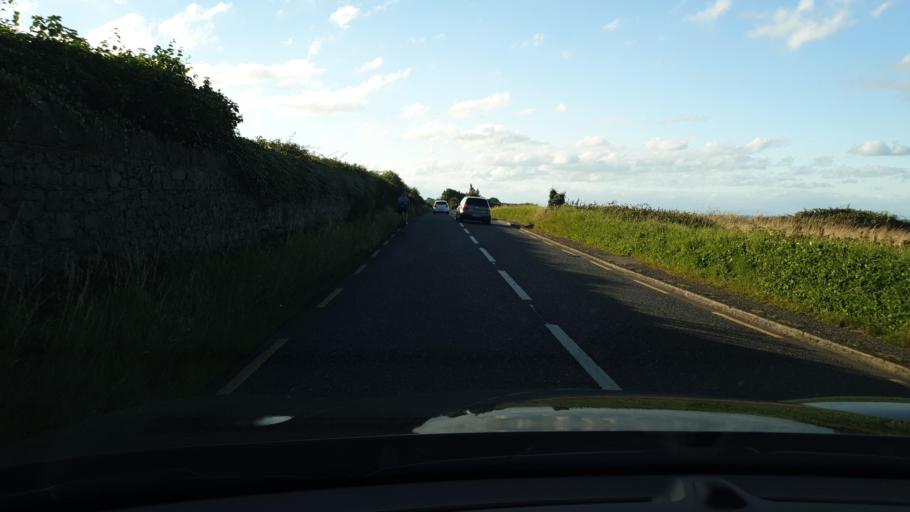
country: IE
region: Leinster
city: Balrothery
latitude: 53.5945
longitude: -6.1596
